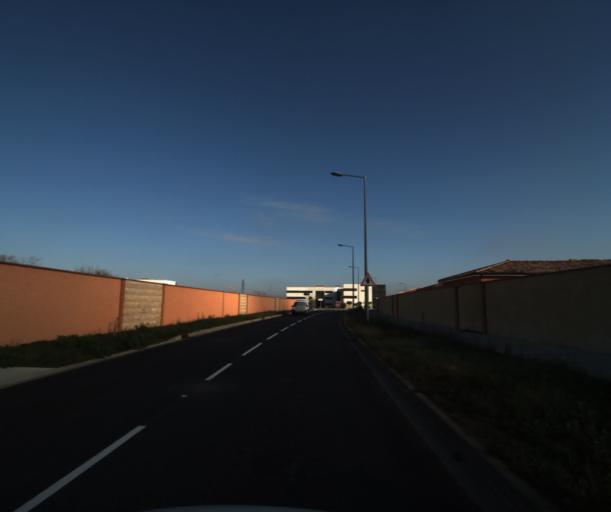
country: FR
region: Midi-Pyrenees
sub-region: Departement de la Haute-Garonne
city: Colomiers
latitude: 43.5984
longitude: 1.3553
